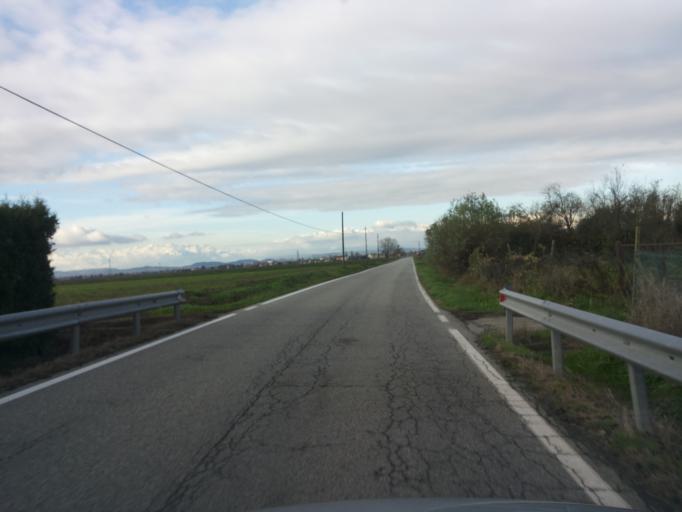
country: IT
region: Piedmont
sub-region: Provincia di Vercelli
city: Crova
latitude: 45.3260
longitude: 8.1912
